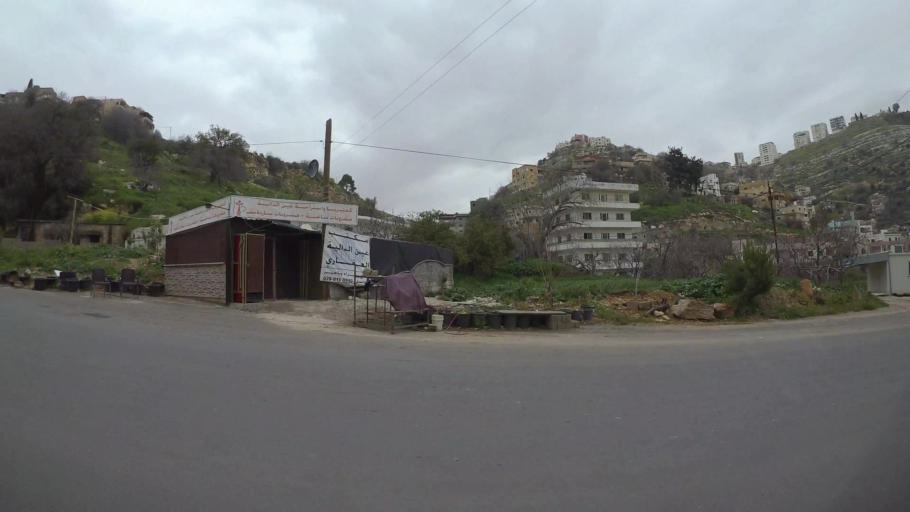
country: JO
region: Amman
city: Wadi as Sir
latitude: 31.9589
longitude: 35.8148
